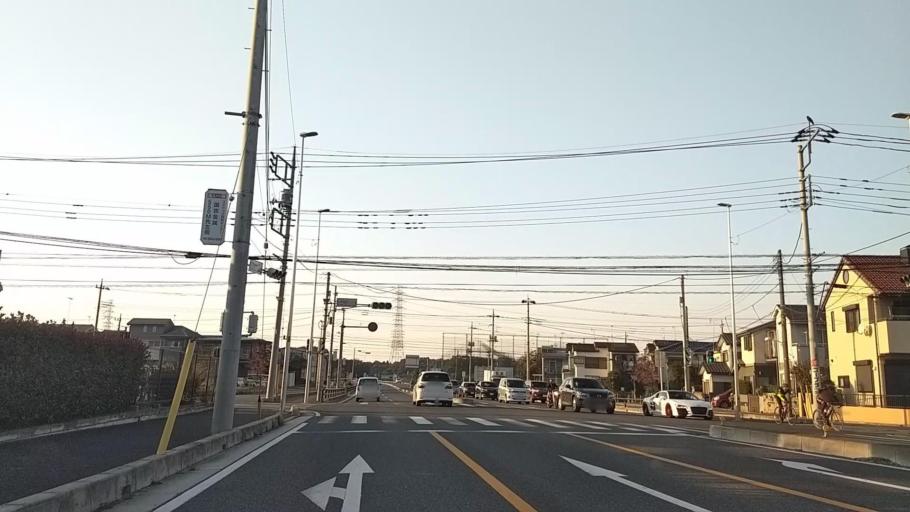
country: JP
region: Saitama
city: Tokorozawa
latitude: 35.8360
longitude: 139.4642
